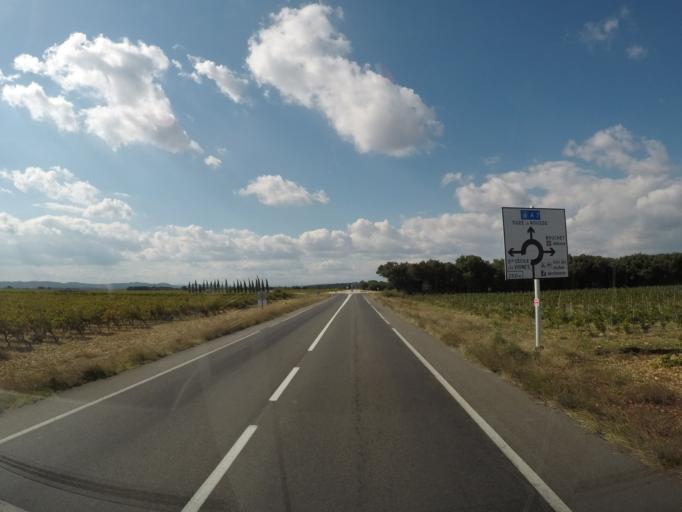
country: FR
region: Rhone-Alpes
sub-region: Departement de la Drome
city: Suze-la-Rousse
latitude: 44.2851
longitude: 4.8753
